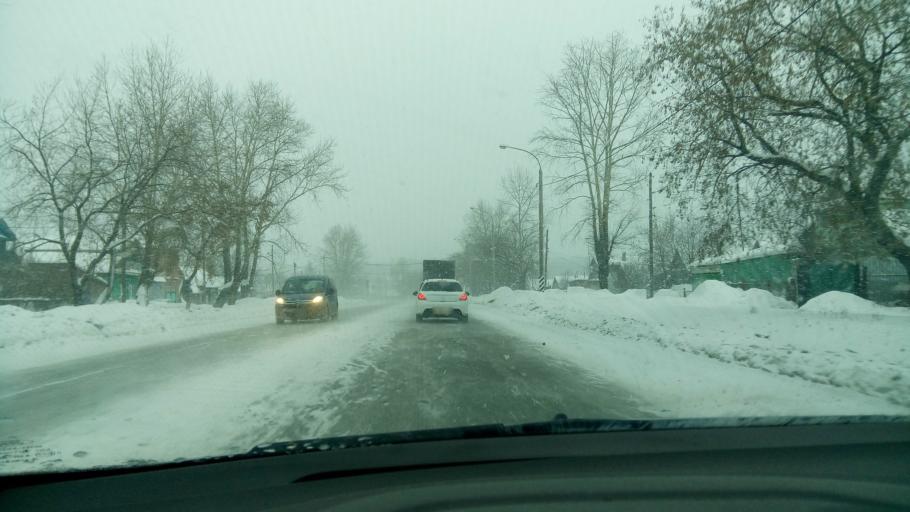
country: RU
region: Sverdlovsk
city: Beloyarskiy
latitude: 56.7659
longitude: 61.4259
